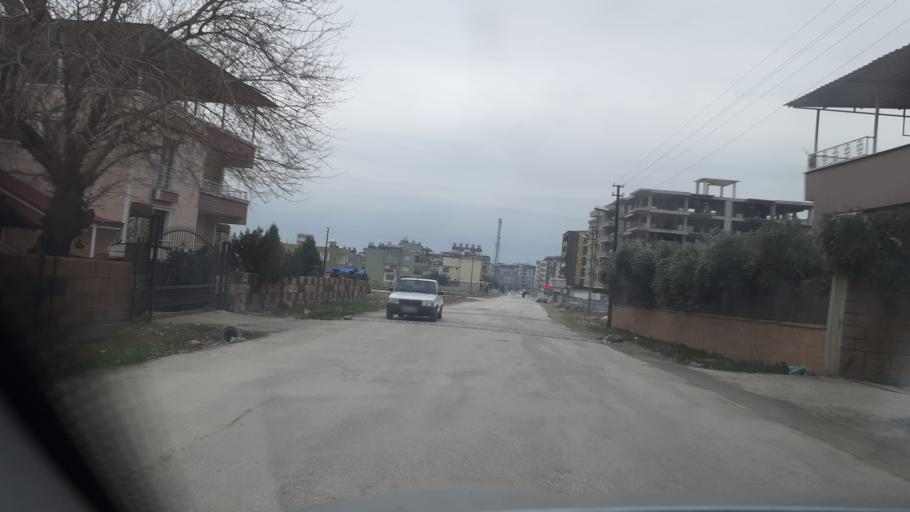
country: TR
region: Hatay
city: Kirikhan
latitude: 36.4863
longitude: 36.3557
